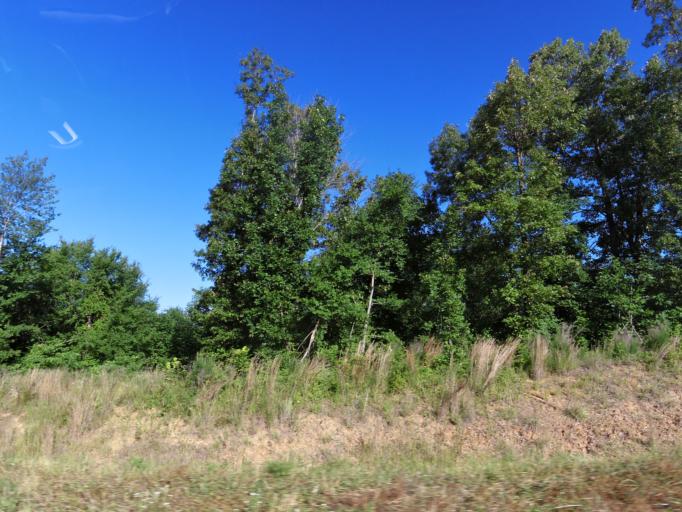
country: US
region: Missouri
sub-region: Butler County
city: Poplar Bluff
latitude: 36.6839
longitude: -90.4875
